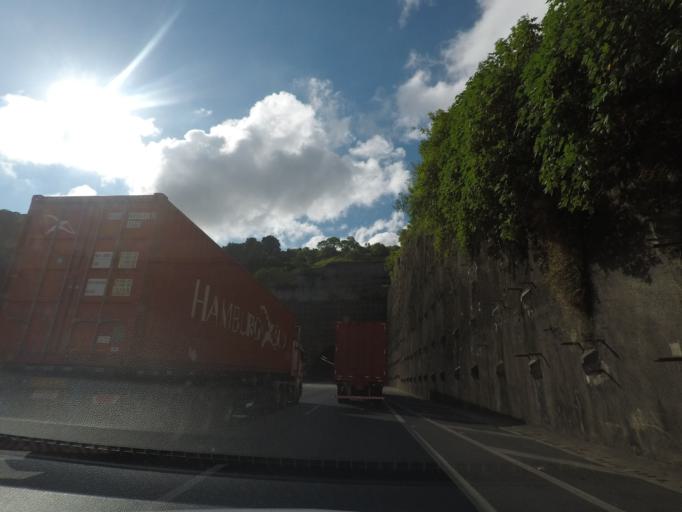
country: BR
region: Sao Paulo
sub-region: Embu
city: Embu
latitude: -23.6260
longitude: -46.8293
